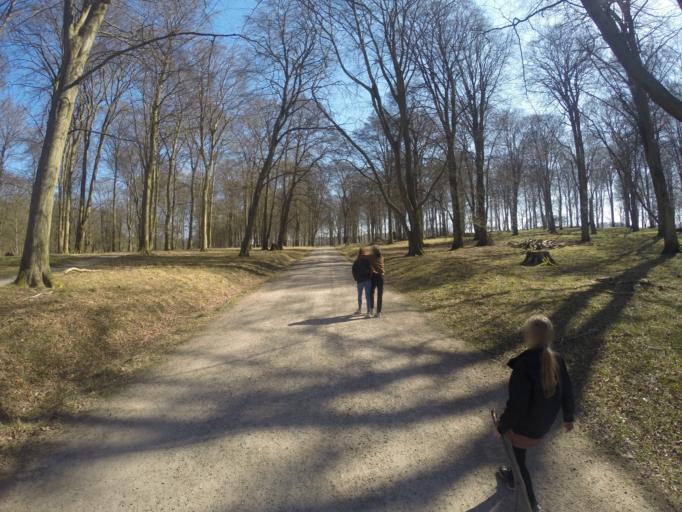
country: DK
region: Capital Region
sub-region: Rudersdal Kommune
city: Trorod
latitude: 55.8030
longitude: 12.5639
